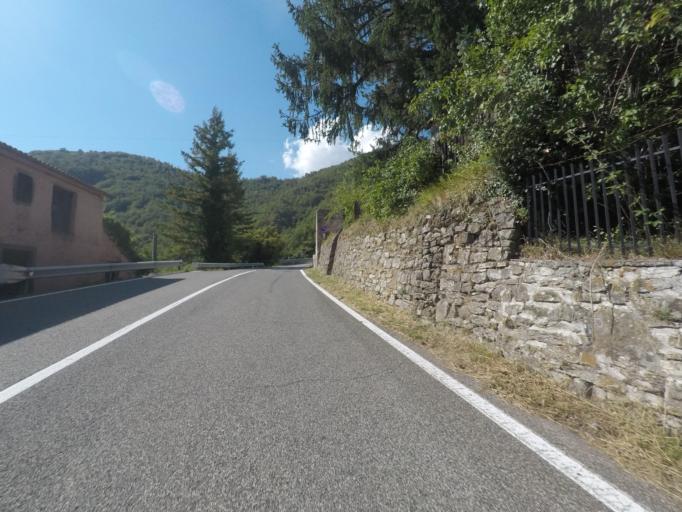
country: IT
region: Tuscany
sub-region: Provincia di Massa-Carrara
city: Fivizzano
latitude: 44.2569
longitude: 10.1727
